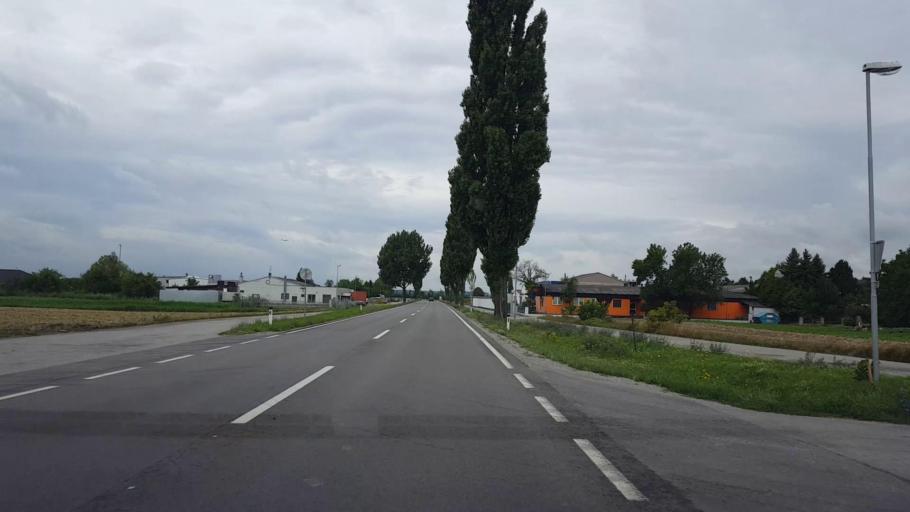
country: AT
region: Lower Austria
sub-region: Politischer Bezirk Bruck an der Leitha
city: Trautmannsdorf an der Leitha
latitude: 48.0508
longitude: 16.6447
